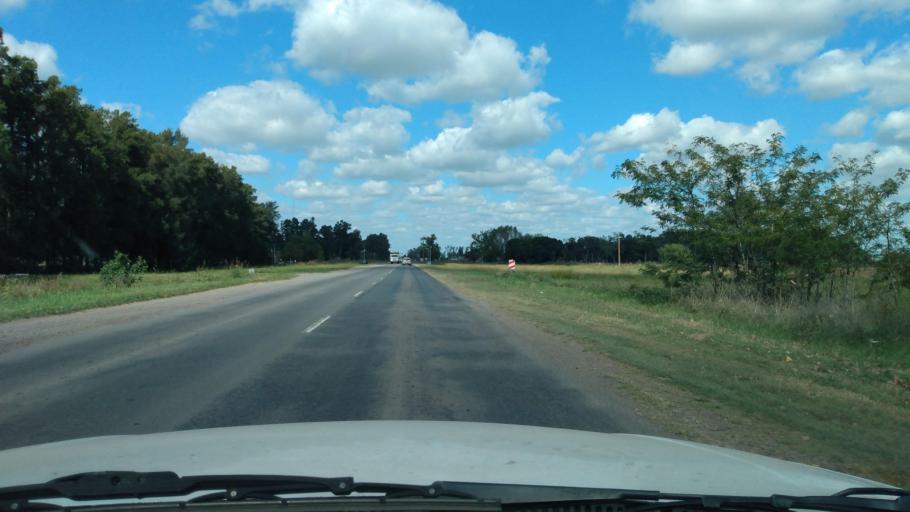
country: AR
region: Buenos Aires
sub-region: Partido de Navarro
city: Navarro
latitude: -34.9916
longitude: -59.3150
